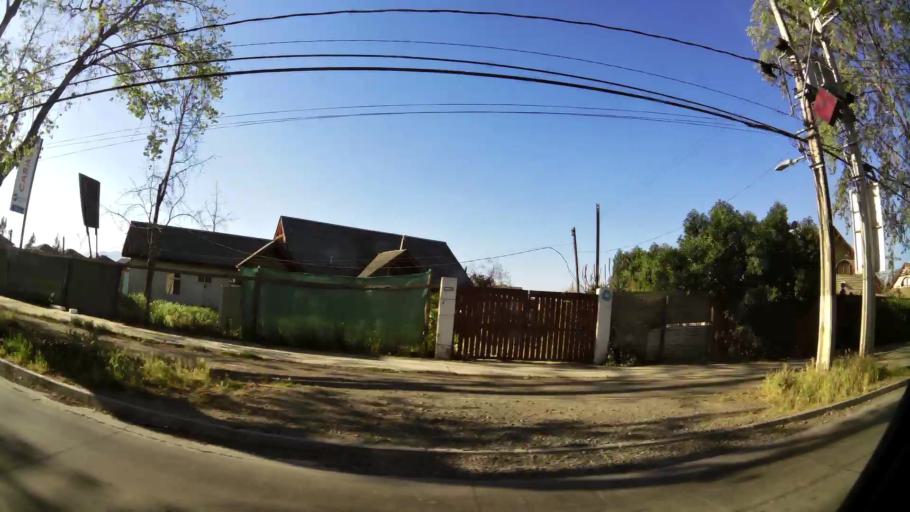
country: CL
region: Santiago Metropolitan
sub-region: Provincia de Talagante
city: Penaflor
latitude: -33.6009
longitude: -70.8627
